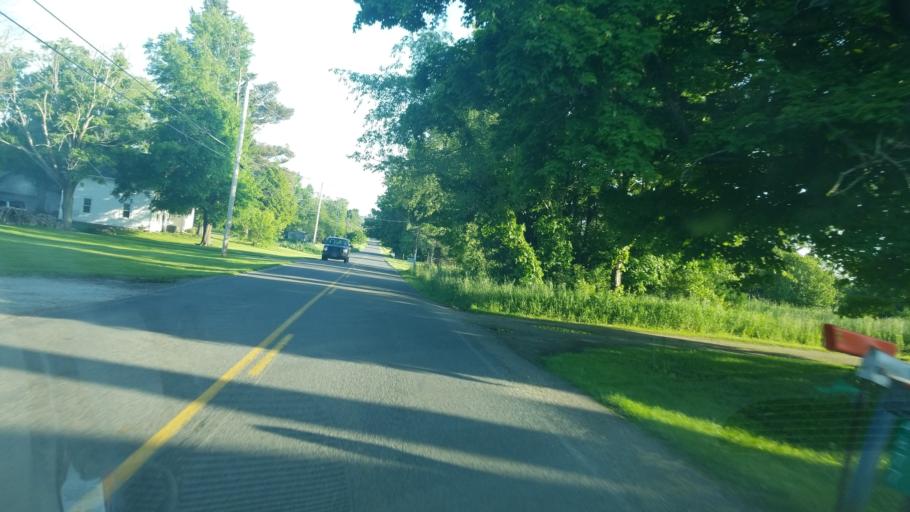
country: US
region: Ohio
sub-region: Portage County
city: Ravenna
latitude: 41.1168
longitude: -81.1460
